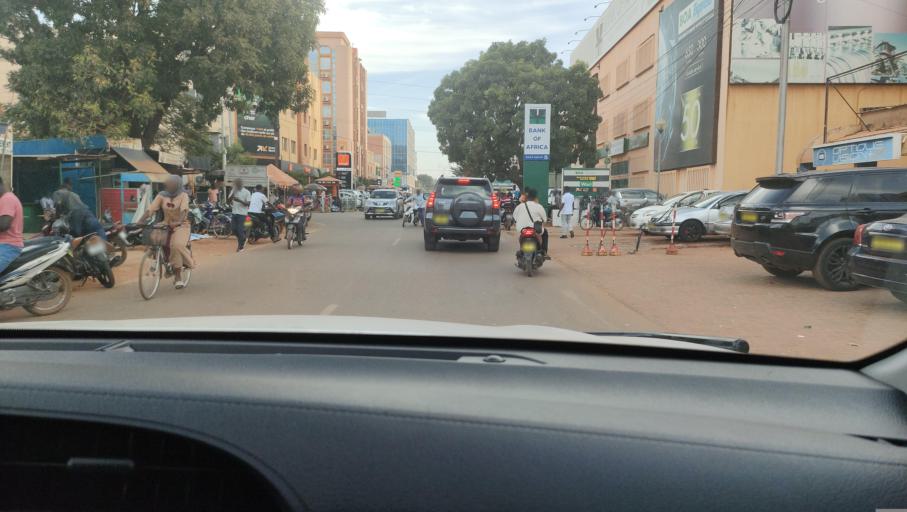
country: BF
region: Centre
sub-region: Kadiogo Province
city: Ouagadougou
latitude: 12.3676
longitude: -1.5152
